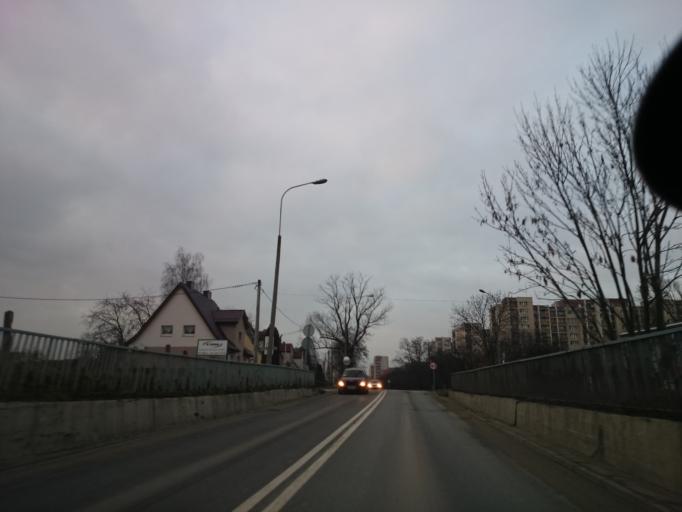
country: PL
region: Opole Voivodeship
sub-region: Powiat opolski
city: Opole
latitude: 50.6616
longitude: 17.9037
